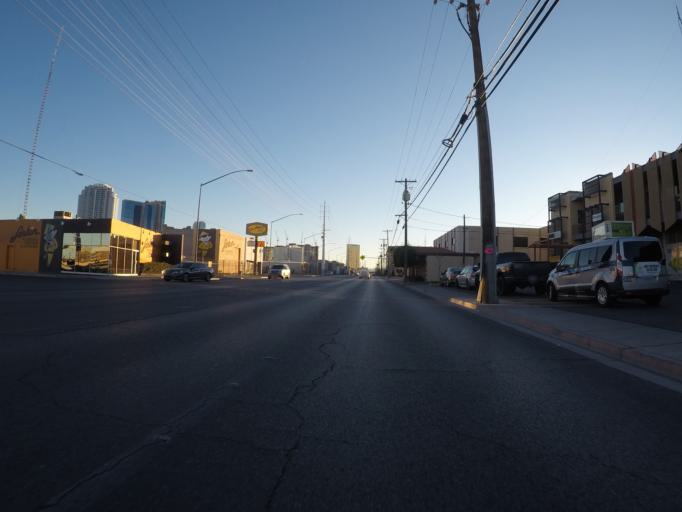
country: US
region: Nevada
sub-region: Clark County
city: Las Vegas
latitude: 36.1505
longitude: -115.1607
